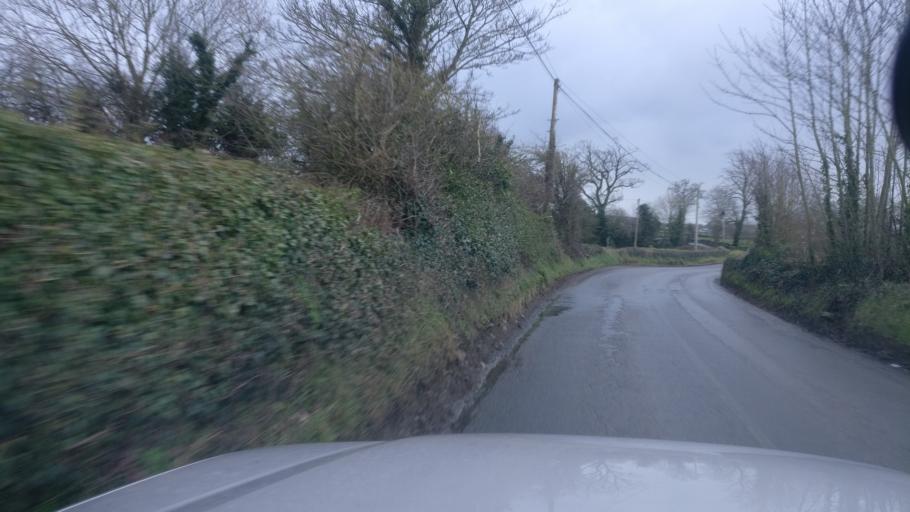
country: IE
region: Munster
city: Nenagh Bridge
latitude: 52.9854
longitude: -8.1087
